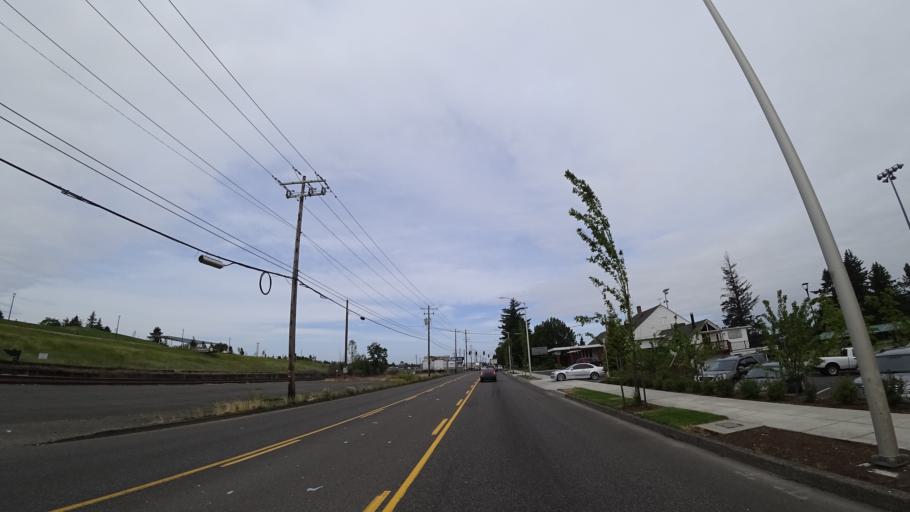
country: US
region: Oregon
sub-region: Multnomah County
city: Lents
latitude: 45.5662
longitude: -122.5865
